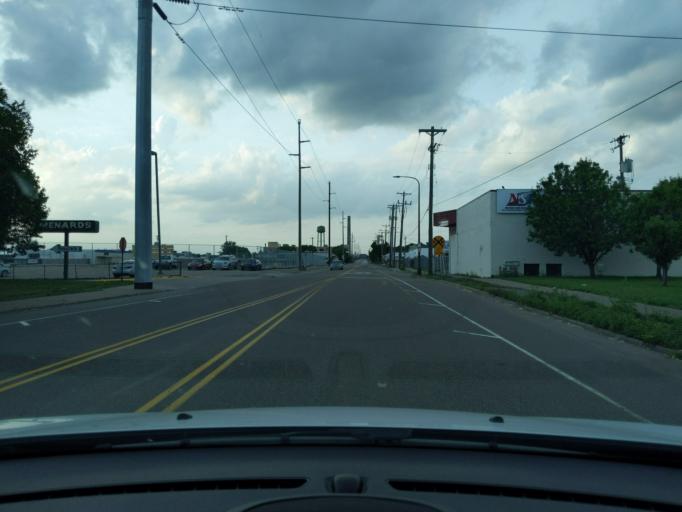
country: US
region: Minnesota
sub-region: Ramsey County
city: Falcon Heights
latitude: 44.9592
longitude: -93.1822
